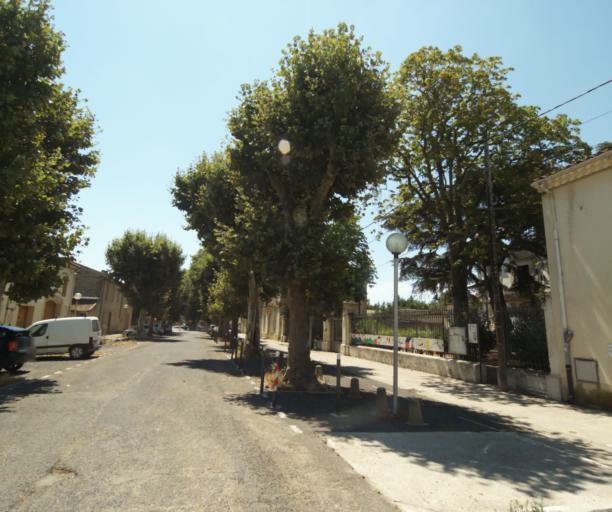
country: FR
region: Languedoc-Roussillon
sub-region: Departement de l'Herault
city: Marsillargues
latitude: 43.6676
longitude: 4.1754
